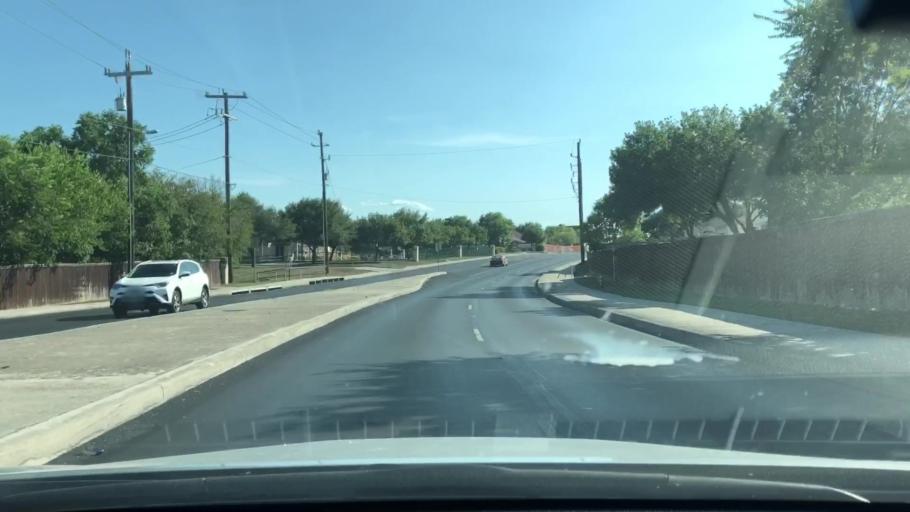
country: US
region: Texas
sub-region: Bexar County
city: Kirby
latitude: 29.4727
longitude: -98.3462
